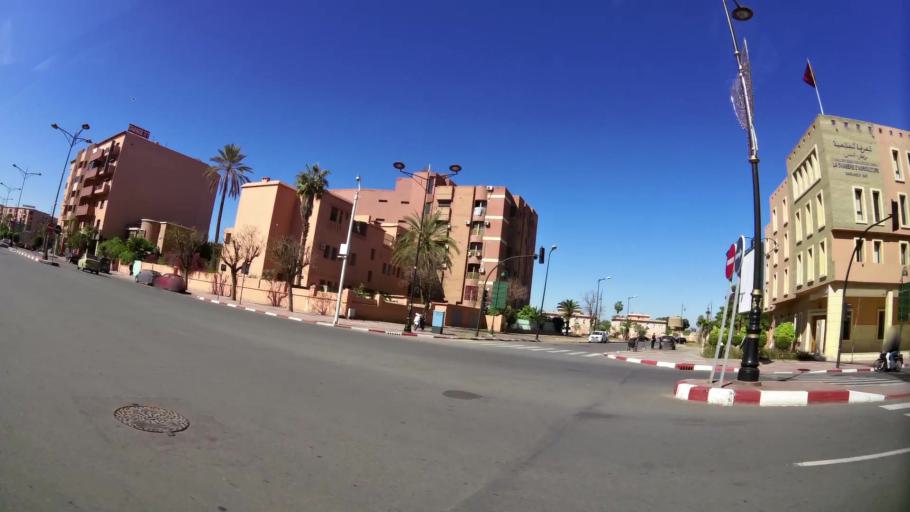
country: MA
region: Marrakech-Tensift-Al Haouz
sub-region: Marrakech
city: Marrakesh
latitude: 31.6326
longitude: -8.0165
